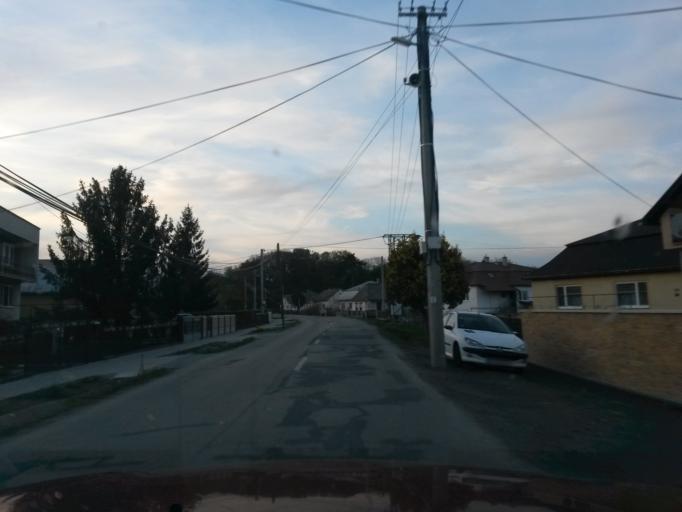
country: HU
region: Borsod-Abauj-Zemplen
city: Satoraljaujhely
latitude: 48.5225
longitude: 21.5877
